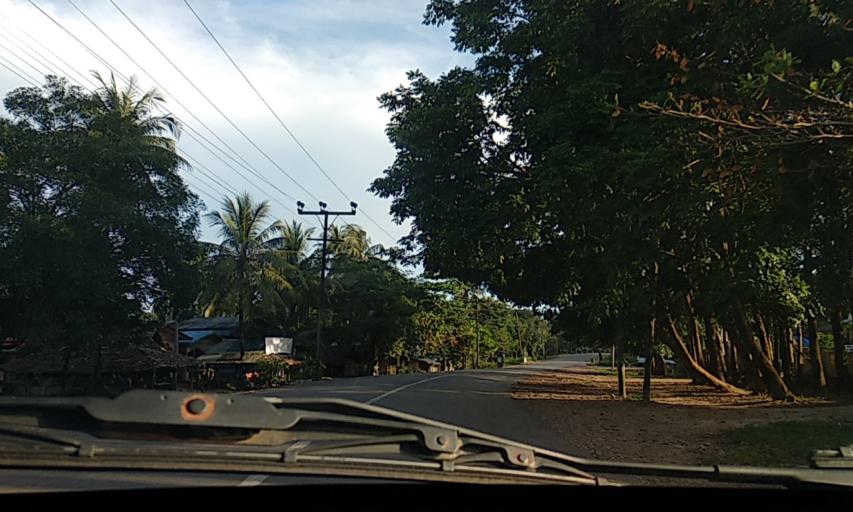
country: MM
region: Mon
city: Mawlamyine
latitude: 16.4012
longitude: 97.7022
